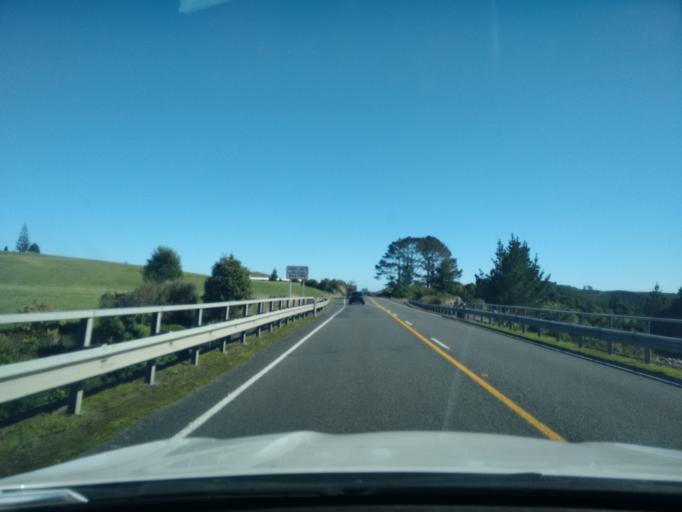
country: NZ
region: Taranaki
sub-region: New Plymouth District
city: New Plymouth
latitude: -39.1412
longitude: 174.1372
